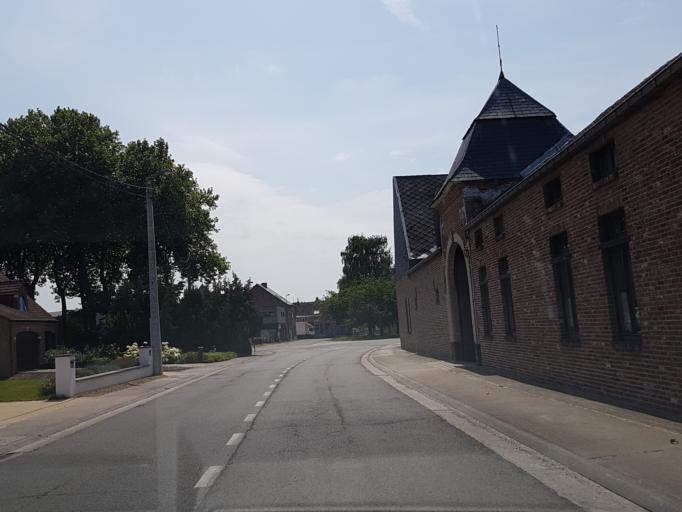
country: BE
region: Flanders
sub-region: Provincie Vlaams-Brabant
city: Kampenhout
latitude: 50.9417
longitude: 4.5645
